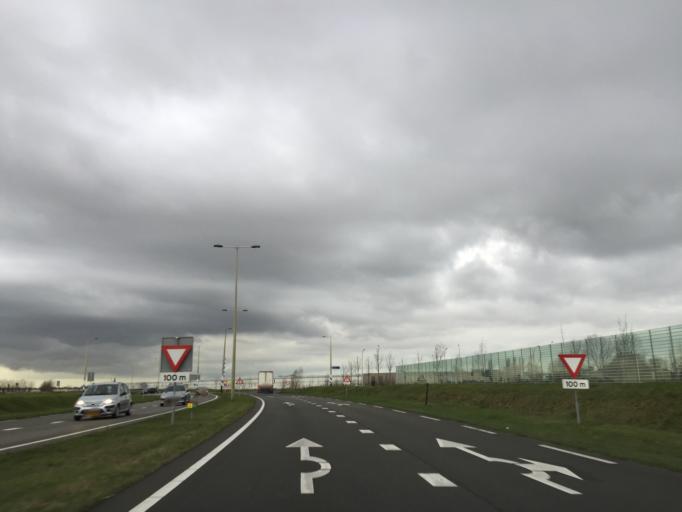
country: NL
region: South Holland
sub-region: Gemeente Pijnacker-Nootdorp
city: Pijnacker
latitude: 52.0041
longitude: 4.4323
